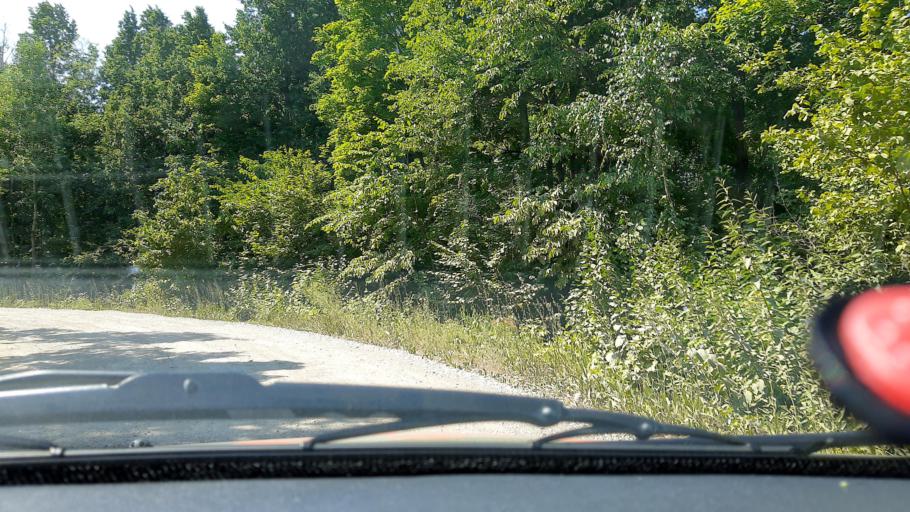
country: RU
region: Bashkortostan
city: Karmaskaly
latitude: 54.3867
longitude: 55.9106
